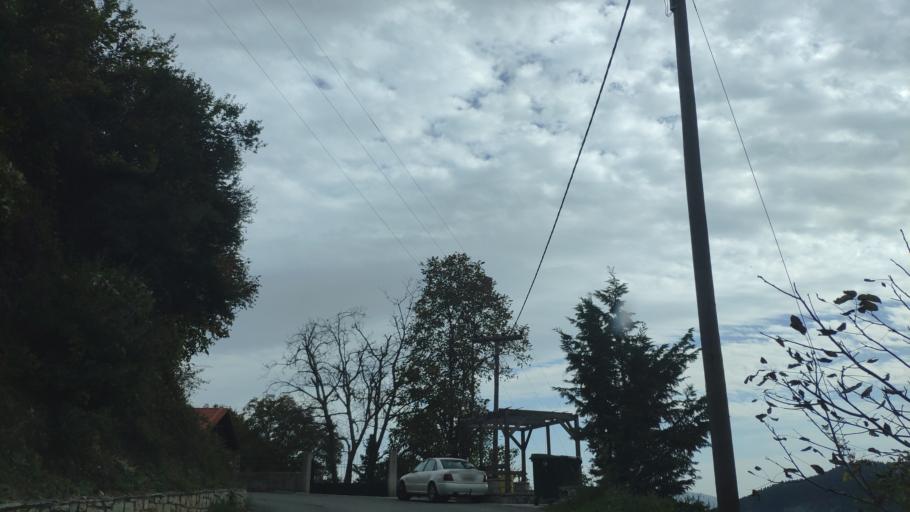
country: GR
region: Central Greece
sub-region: Nomos Fthiotidos
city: Stavros
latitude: 38.7392
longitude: 22.3410
